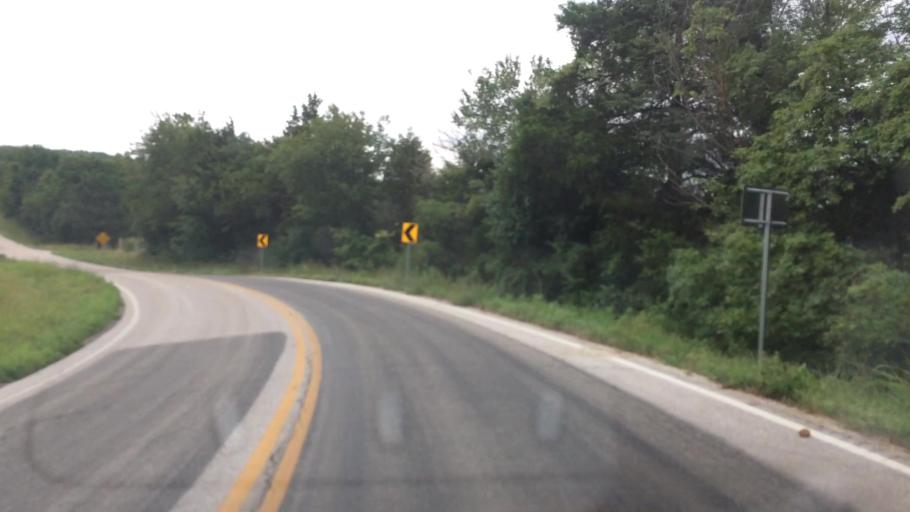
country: US
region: Missouri
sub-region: Webster County
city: Marshfield
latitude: 37.3417
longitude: -93.0199
